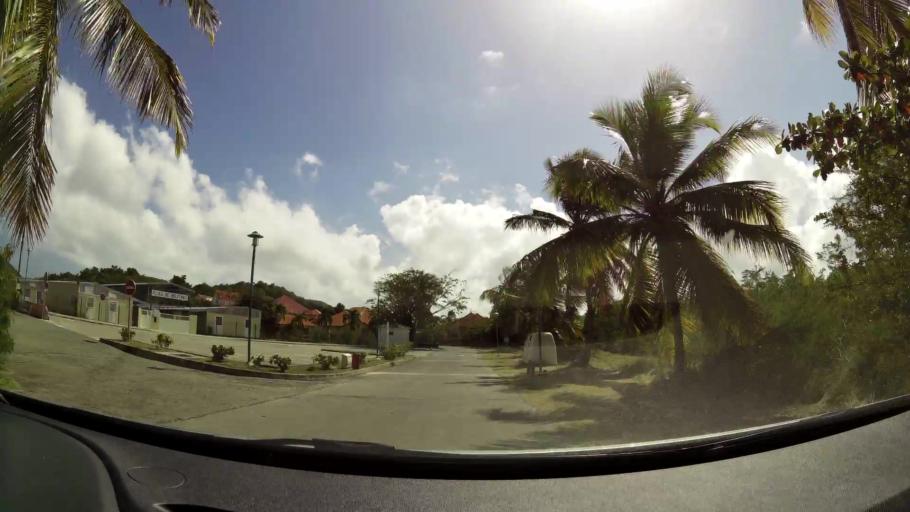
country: MQ
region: Martinique
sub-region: Martinique
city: Le Marin
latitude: 14.4449
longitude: -60.8797
